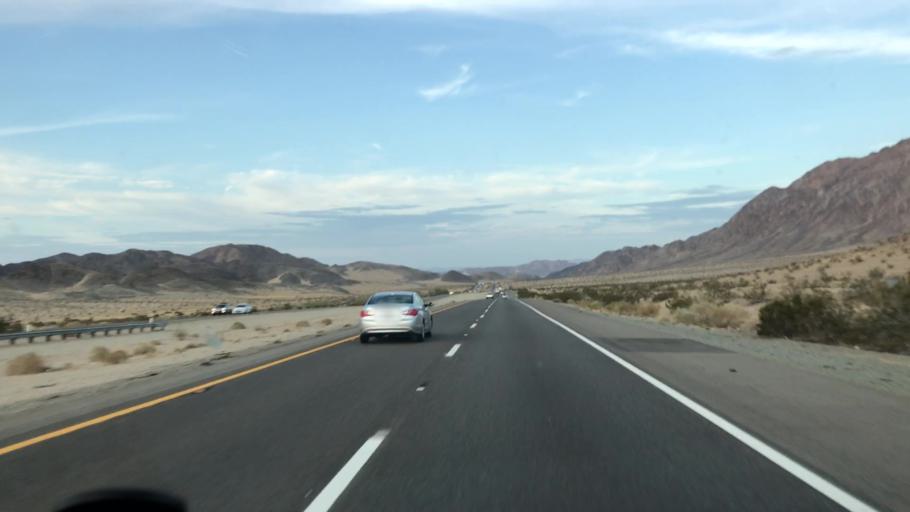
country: US
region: California
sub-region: San Bernardino County
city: Fort Irwin
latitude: 35.0843
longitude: -116.3698
